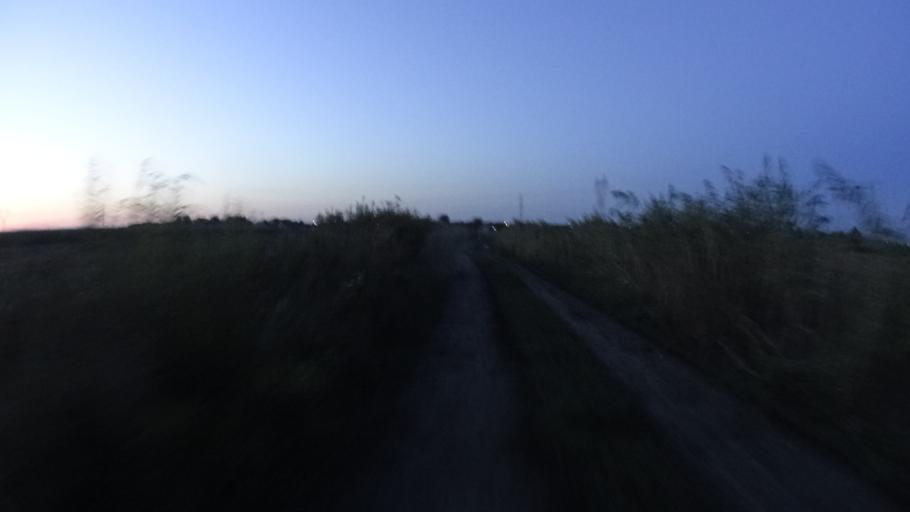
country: PL
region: Masovian Voivodeship
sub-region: Powiat warszawski zachodni
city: Ozarow Mazowiecki
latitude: 52.2253
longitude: 20.7914
